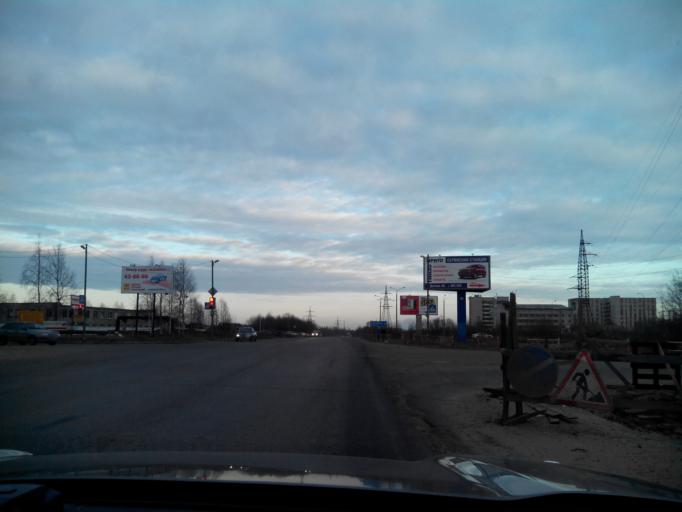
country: RU
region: Arkhangelskaya
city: Arkhangel'sk
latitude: 64.5191
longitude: 40.6765
